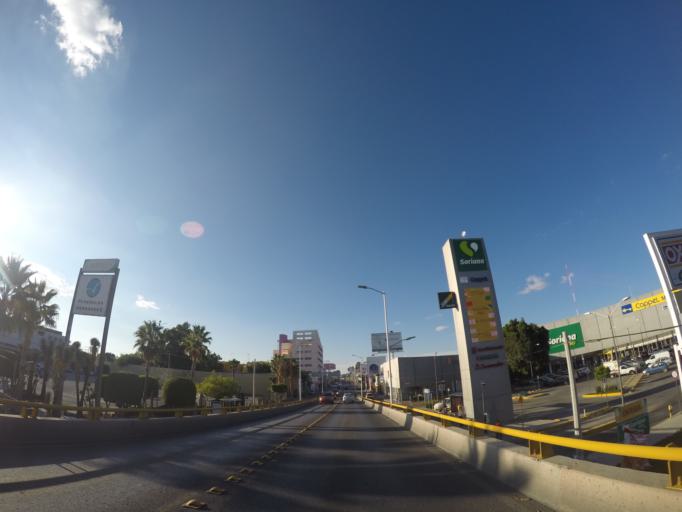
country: MX
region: San Luis Potosi
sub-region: San Luis Potosi
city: San Luis Potosi
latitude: 22.1607
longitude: -101.0003
